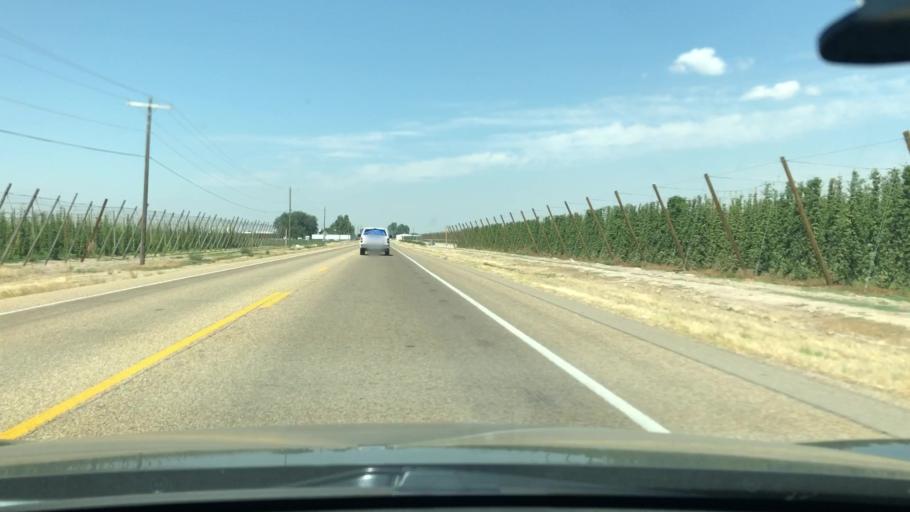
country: US
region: Idaho
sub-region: Canyon County
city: Wilder
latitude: 43.6848
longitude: -116.9120
